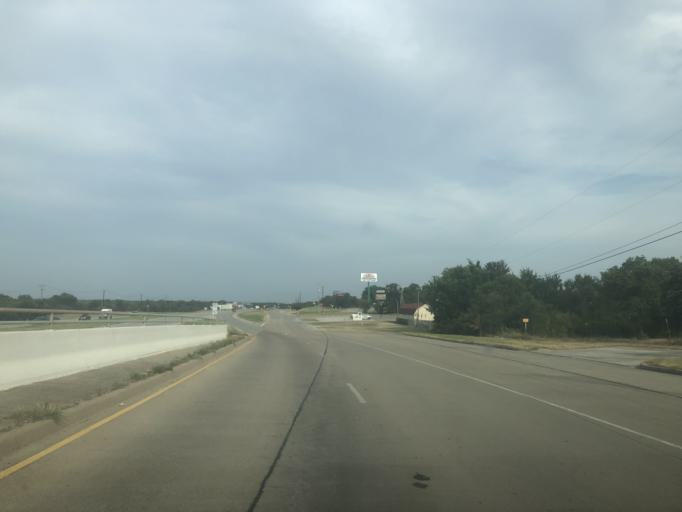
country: US
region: Texas
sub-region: Tarrant County
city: Lakeside
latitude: 32.8246
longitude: -97.4772
